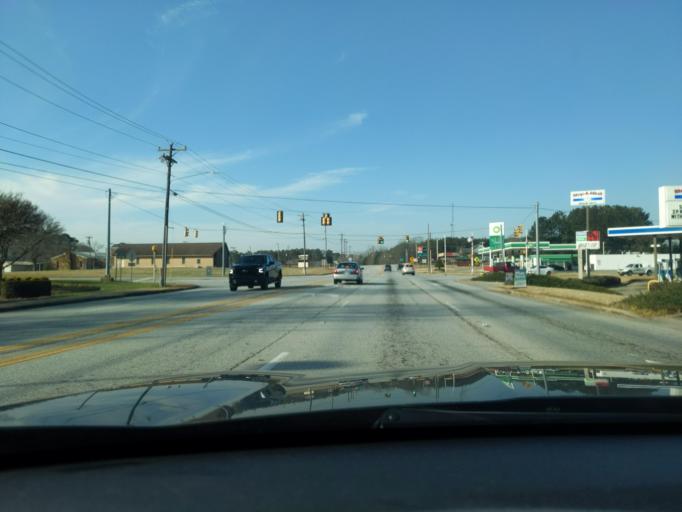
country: US
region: South Carolina
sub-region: Greenwood County
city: Greenwood
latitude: 34.2030
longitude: -82.1984
